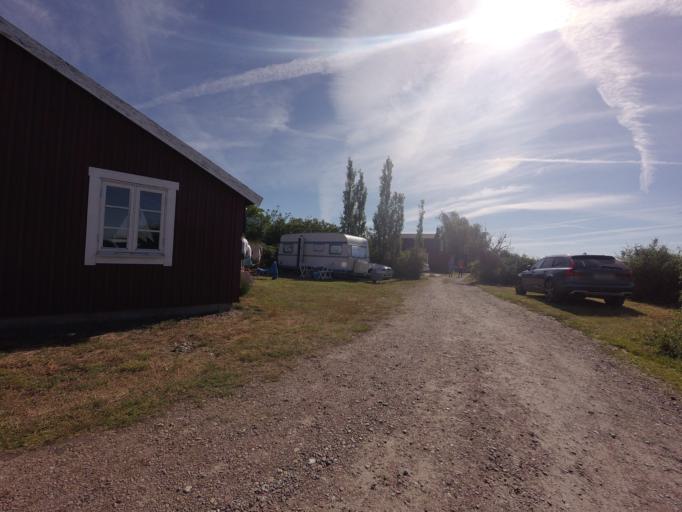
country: SE
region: Skane
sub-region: Trelleborgs Kommun
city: Skare
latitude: 55.3760
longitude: 13.0499
